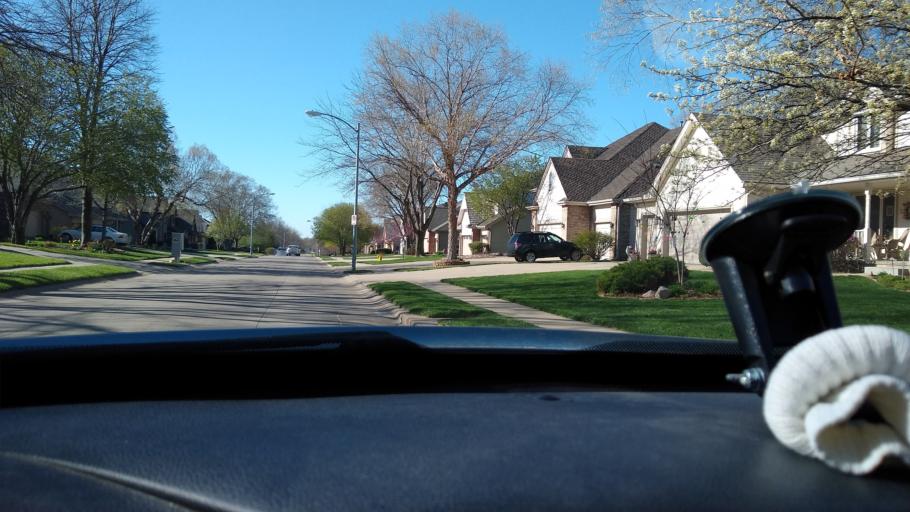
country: US
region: Nebraska
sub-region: Douglas County
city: Ralston
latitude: 41.1967
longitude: -96.0724
